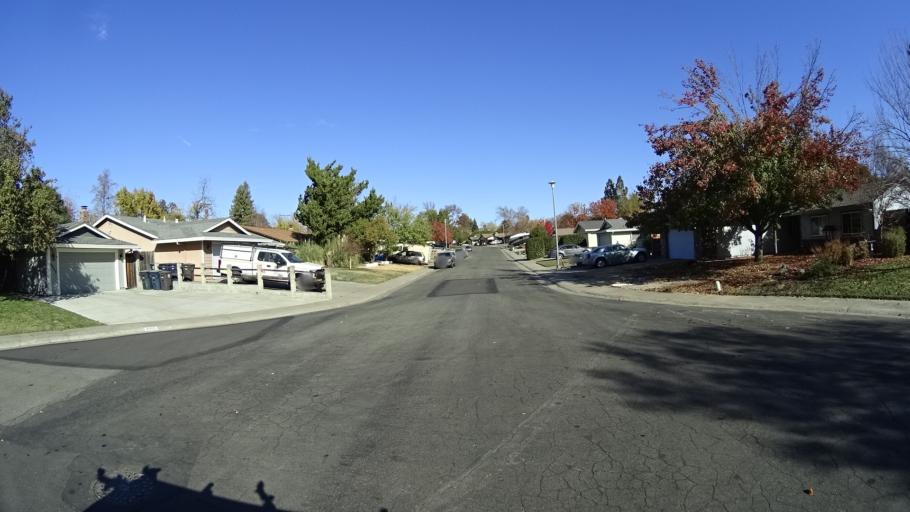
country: US
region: California
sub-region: Sacramento County
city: Citrus Heights
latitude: 38.6748
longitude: -121.3000
